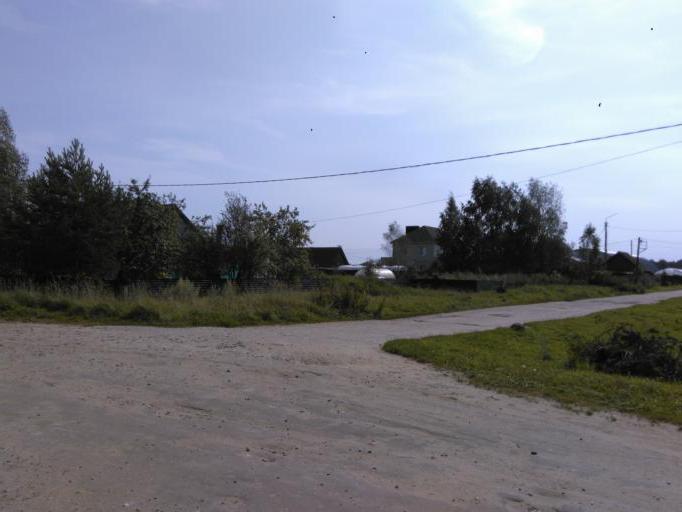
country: RU
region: Kostroma
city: Volgorechensk
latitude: 57.5798
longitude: 41.0599
